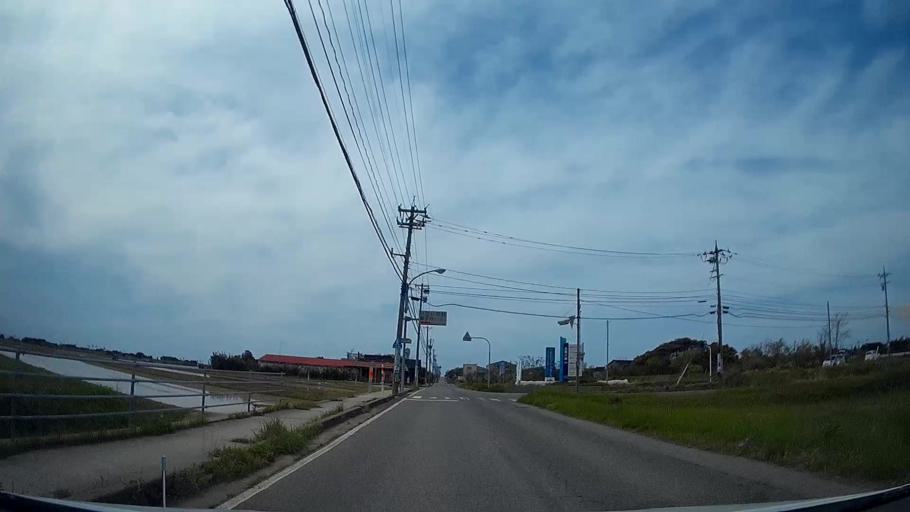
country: JP
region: Ishikawa
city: Hakui
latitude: 37.0128
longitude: 136.7583
